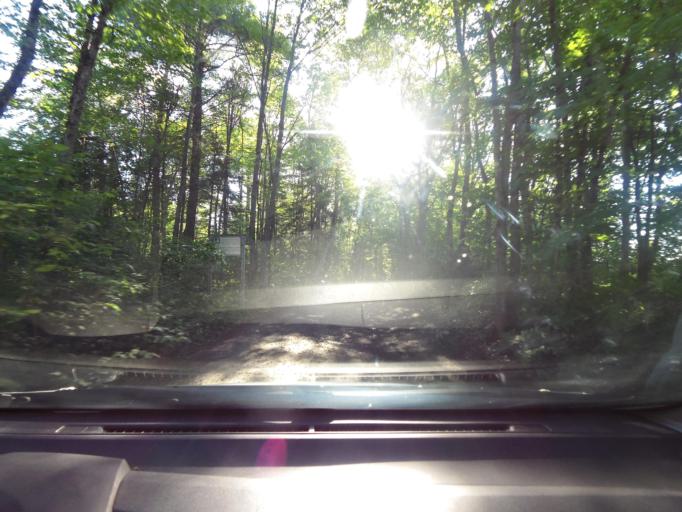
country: CA
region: Quebec
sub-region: Mauricie
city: Becancour
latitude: 46.5453
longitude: -72.4031
